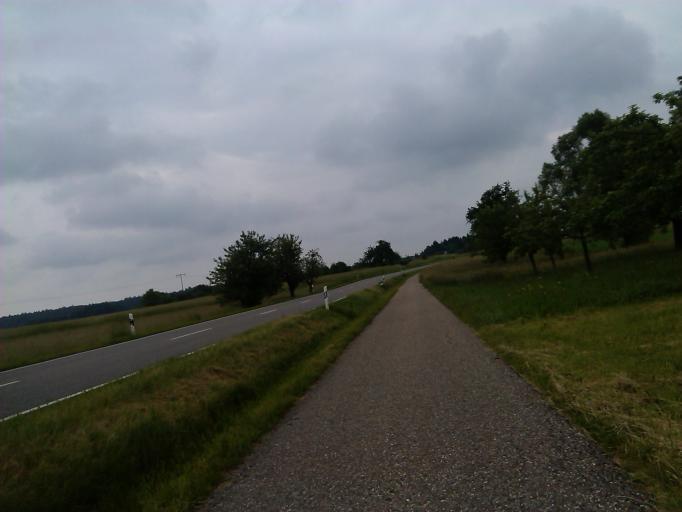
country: DE
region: Baden-Wuerttemberg
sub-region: Regierungsbezirk Stuttgart
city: Wustenrot
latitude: 49.0927
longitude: 9.4830
